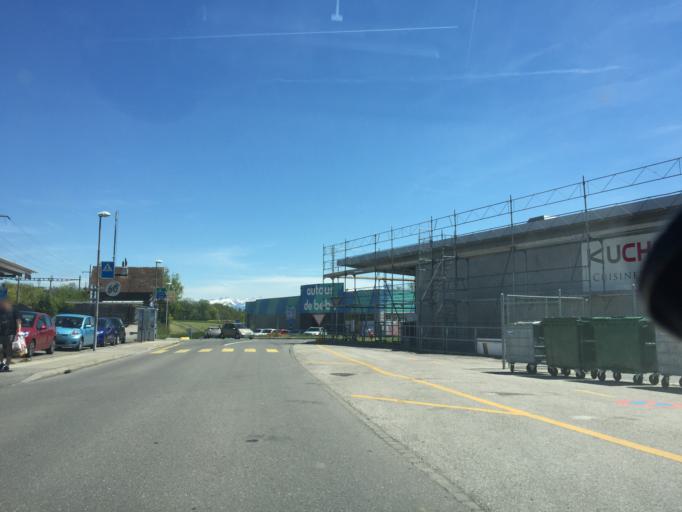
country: CH
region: Vaud
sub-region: Morges District
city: Saint-Prex
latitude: 46.4751
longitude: 6.4258
